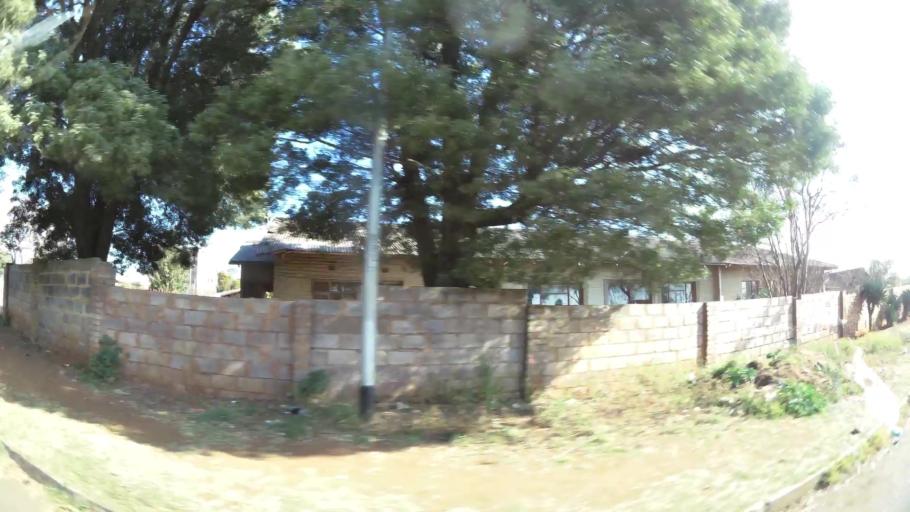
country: ZA
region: Gauteng
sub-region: West Rand District Municipality
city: Randfontein
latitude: -26.1839
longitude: 27.6940
